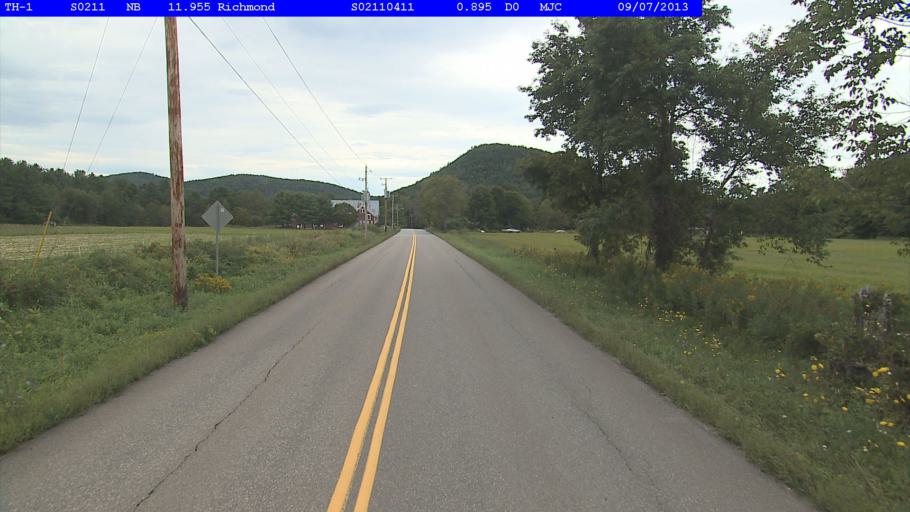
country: US
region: Vermont
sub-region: Chittenden County
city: Williston
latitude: 44.3654
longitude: -72.9966
